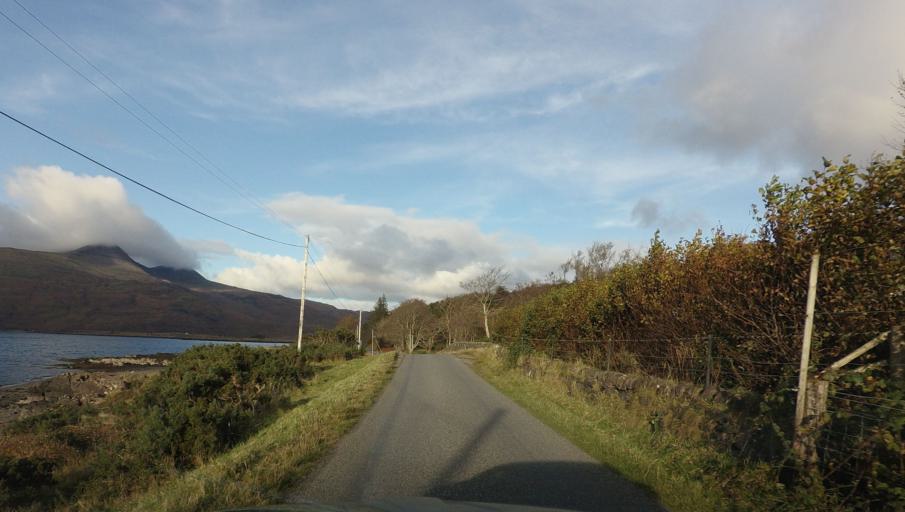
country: GB
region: Scotland
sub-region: Argyll and Bute
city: Isle Of Mull
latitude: 56.3672
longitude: -6.0163
